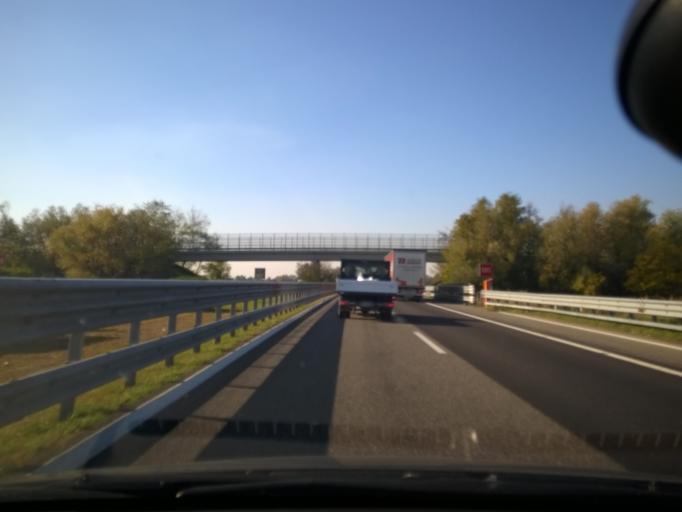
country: IT
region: Emilia-Romagna
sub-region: Provincia di Piacenza
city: Caorso
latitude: 45.0457
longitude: 9.8388
